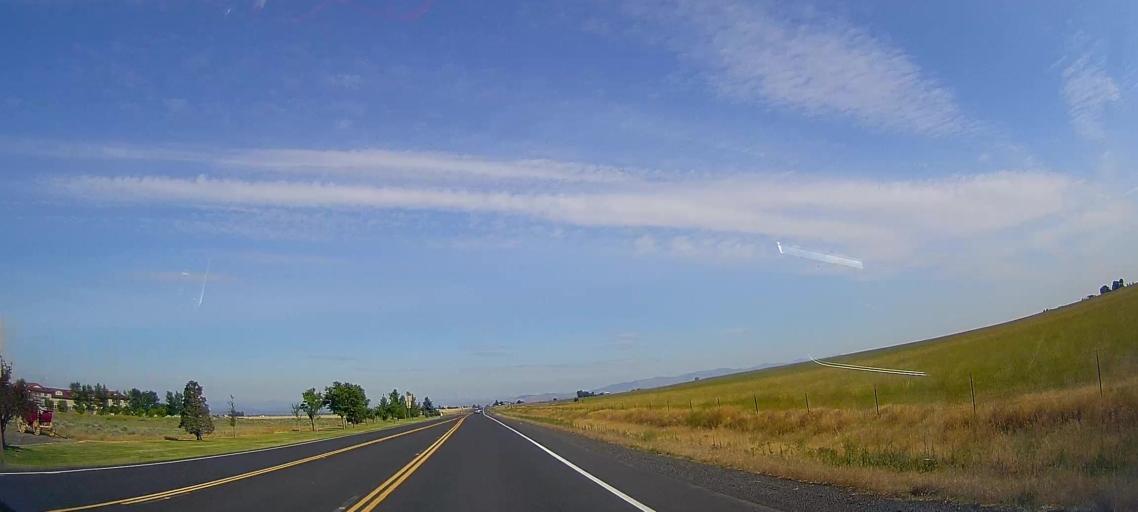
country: US
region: Oregon
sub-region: Jefferson County
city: Madras
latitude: 44.6660
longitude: -121.1376
